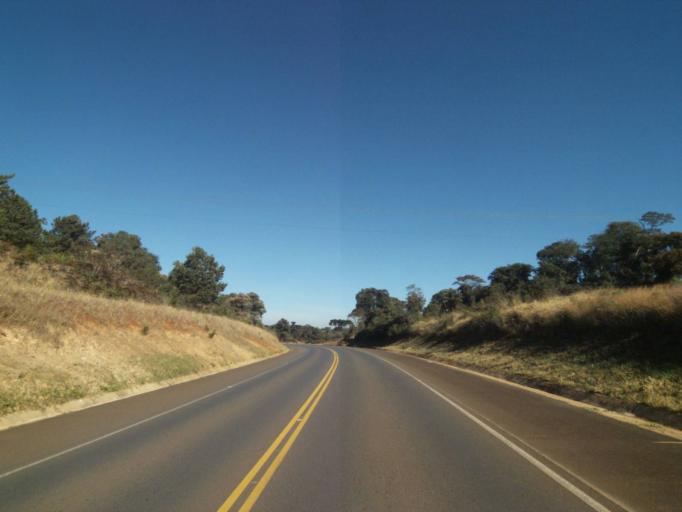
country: BR
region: Parana
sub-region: Tibagi
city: Tibagi
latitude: -24.4232
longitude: -50.3943
